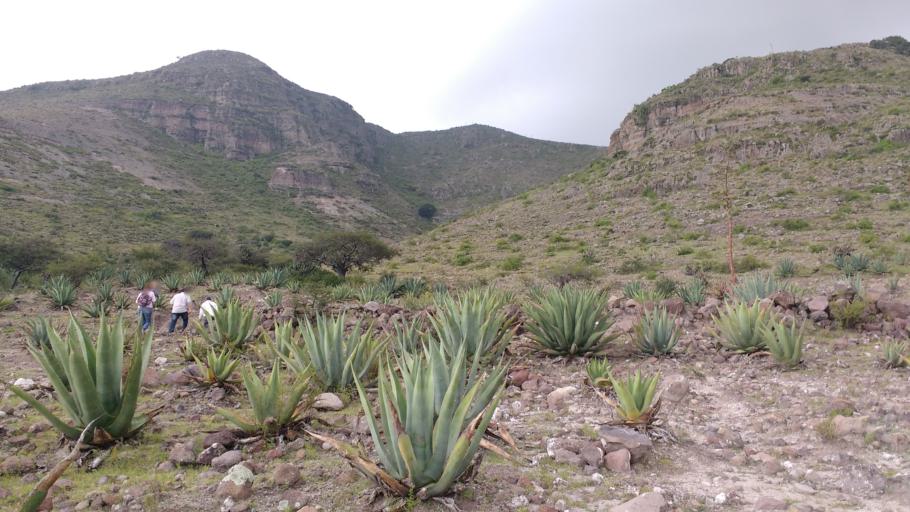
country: MX
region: Hidalgo
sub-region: Tezontepec de Aldama
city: Tenango
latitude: 20.2752
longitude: -99.2942
